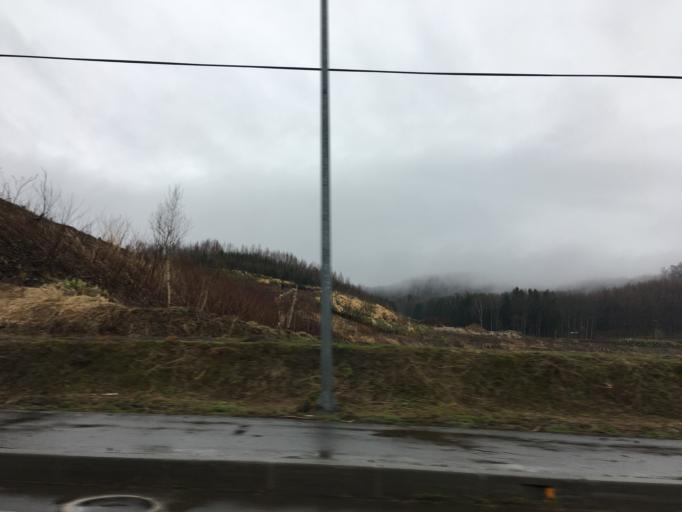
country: JP
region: Hokkaido
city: Nayoro
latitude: 44.0681
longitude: 142.4124
